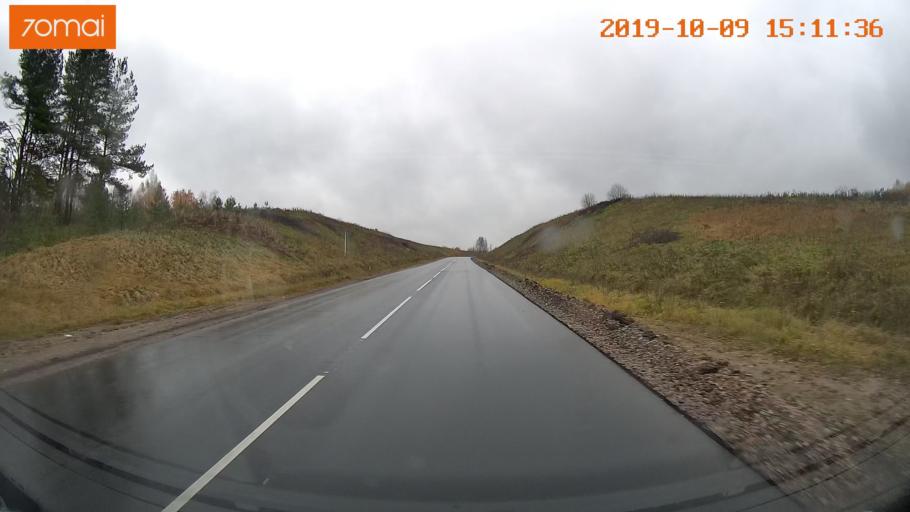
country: RU
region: Kostroma
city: Susanino
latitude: 58.1628
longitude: 41.6292
